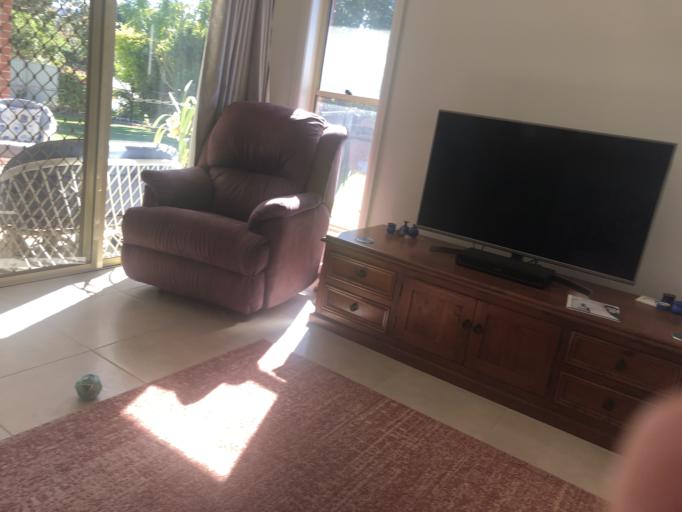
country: AU
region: New South Wales
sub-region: Coffs Harbour
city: Boambee
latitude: -30.3527
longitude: 153.0664
